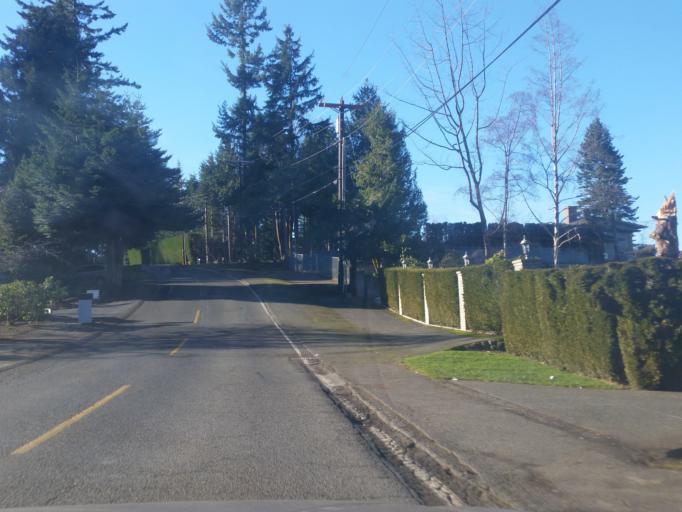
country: US
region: Washington
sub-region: Snohomish County
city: Meadowdale
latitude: 47.8410
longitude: -122.3486
